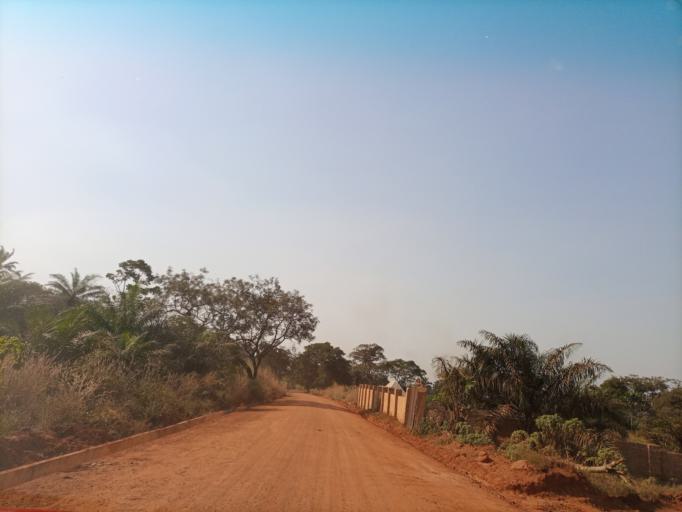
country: NG
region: Enugu
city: Aku
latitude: 6.7039
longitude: 7.3145
